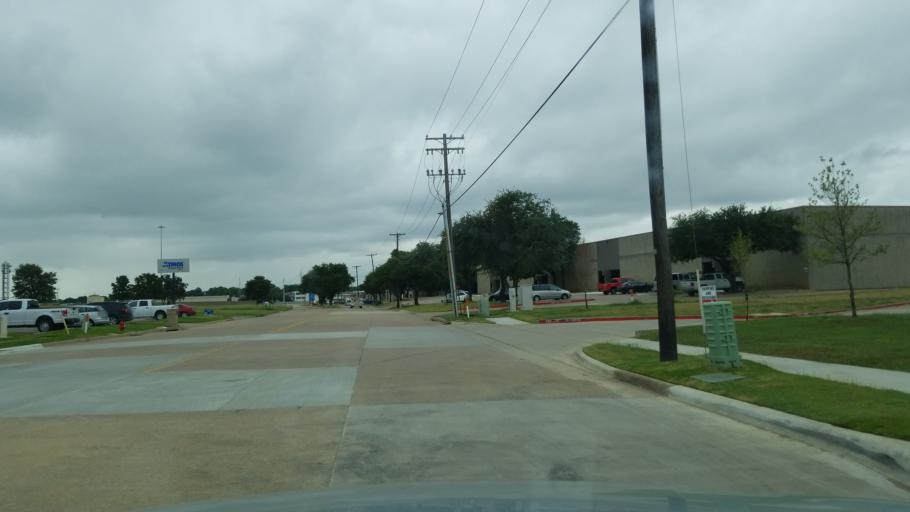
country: US
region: Texas
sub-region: Tarrant County
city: Euless
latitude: 32.8426
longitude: -97.1076
